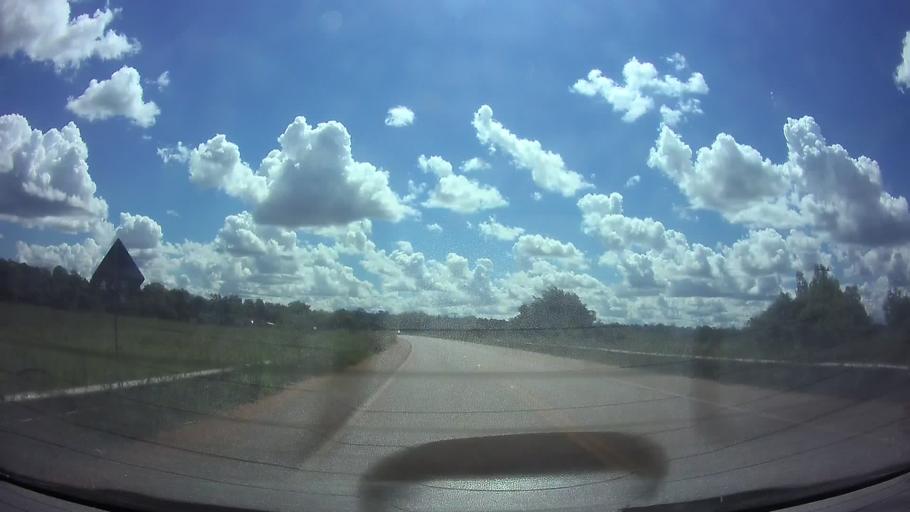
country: PY
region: Paraguari
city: La Colmena
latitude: -25.8984
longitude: -56.7894
